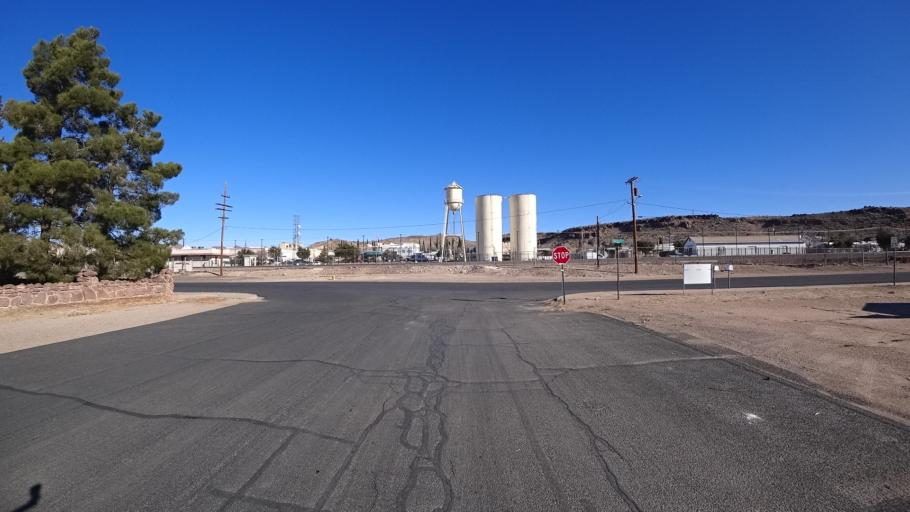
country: US
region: Arizona
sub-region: Mohave County
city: Kingman
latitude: 35.1873
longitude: -114.0516
